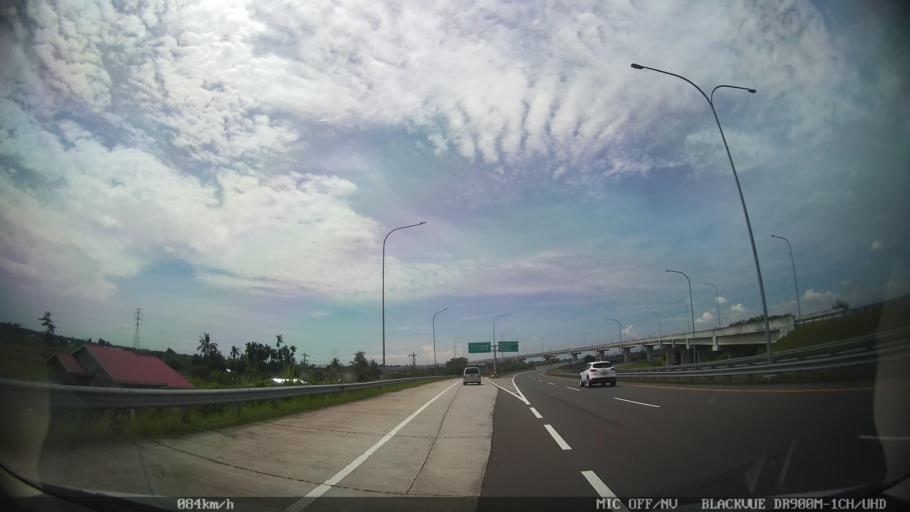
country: ID
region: North Sumatra
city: Percut
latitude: 3.5411
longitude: 98.8550
